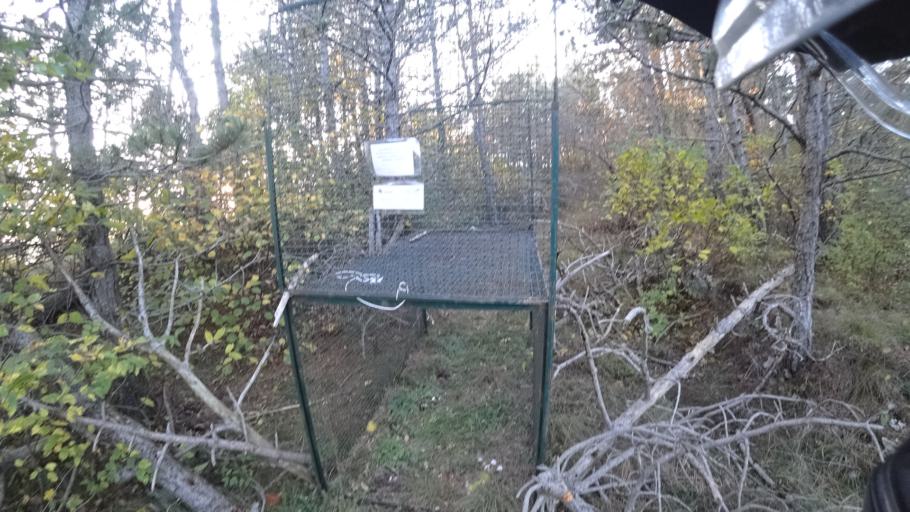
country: HR
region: Primorsko-Goranska
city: Klana
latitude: 45.4969
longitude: 14.4079
